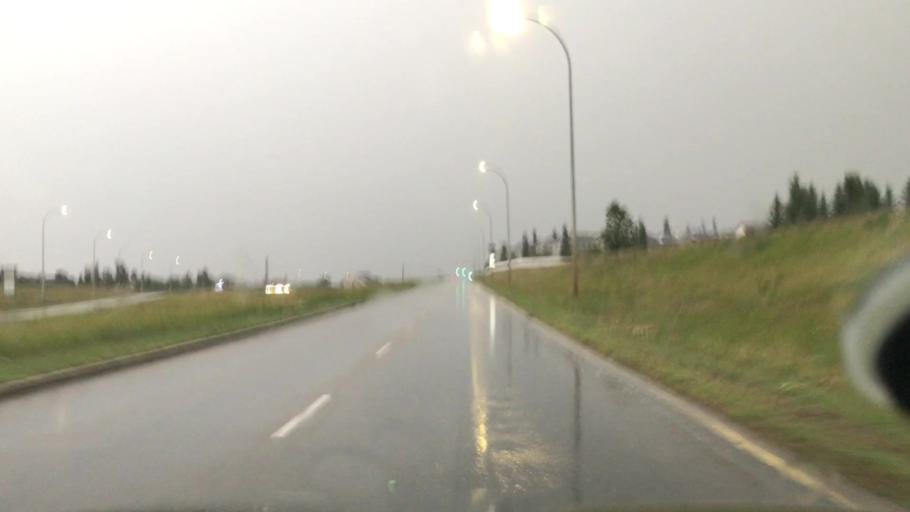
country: CA
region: Alberta
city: Edmonton
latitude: 53.4527
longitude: -113.5894
